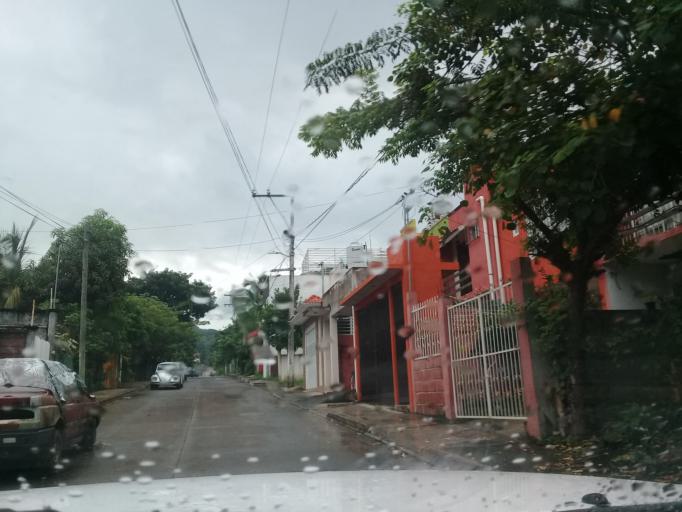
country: MX
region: Veracruz
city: San Andres Tuxtla
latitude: 18.4379
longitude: -95.1934
